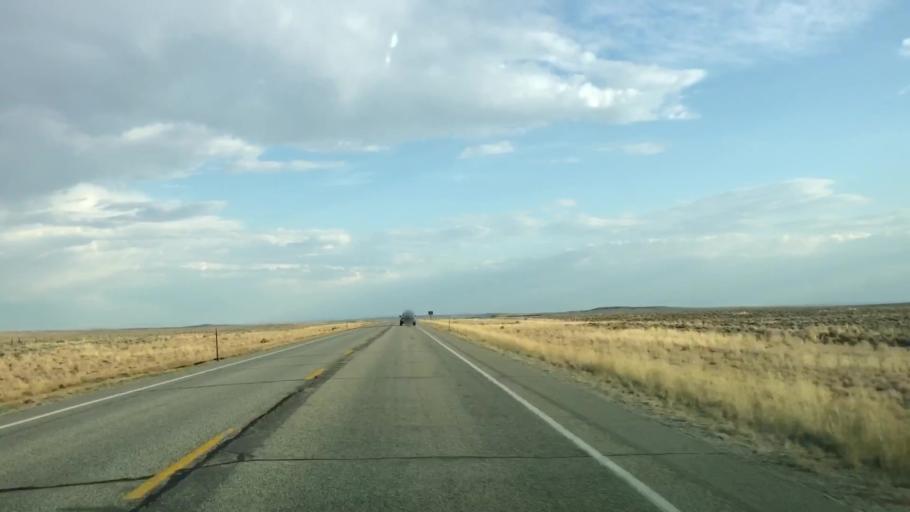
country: US
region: Wyoming
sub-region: Sublette County
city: Pinedale
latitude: 42.3943
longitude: -109.5425
